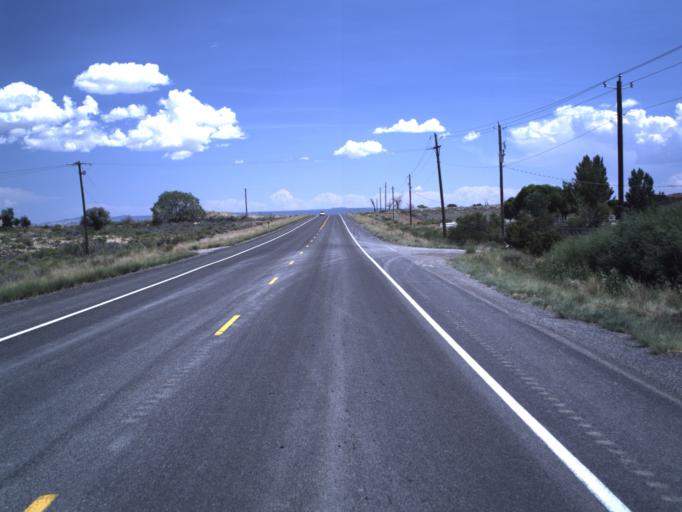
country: US
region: Utah
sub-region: Emery County
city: Huntington
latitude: 39.3436
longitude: -110.9853
